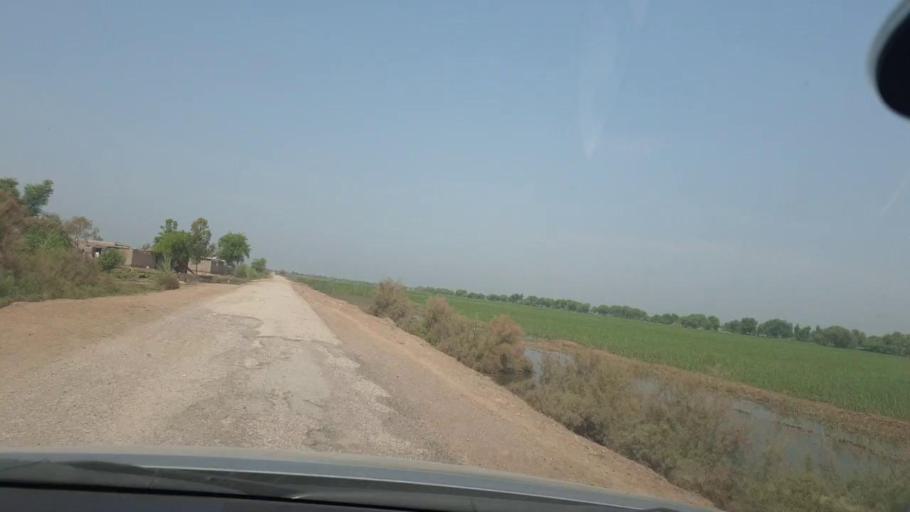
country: PK
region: Balochistan
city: Mehrabpur
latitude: 28.0661
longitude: 68.0600
